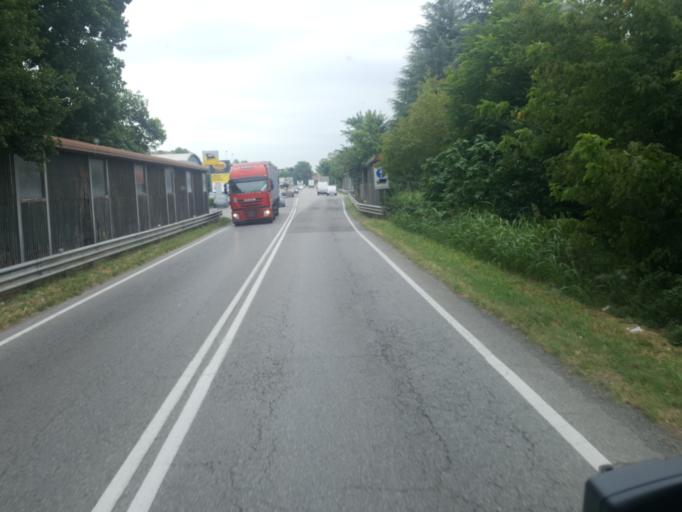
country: IT
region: Lombardy
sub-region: Citta metropolitana di Milano
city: Melzo
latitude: 45.4943
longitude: 9.4207
